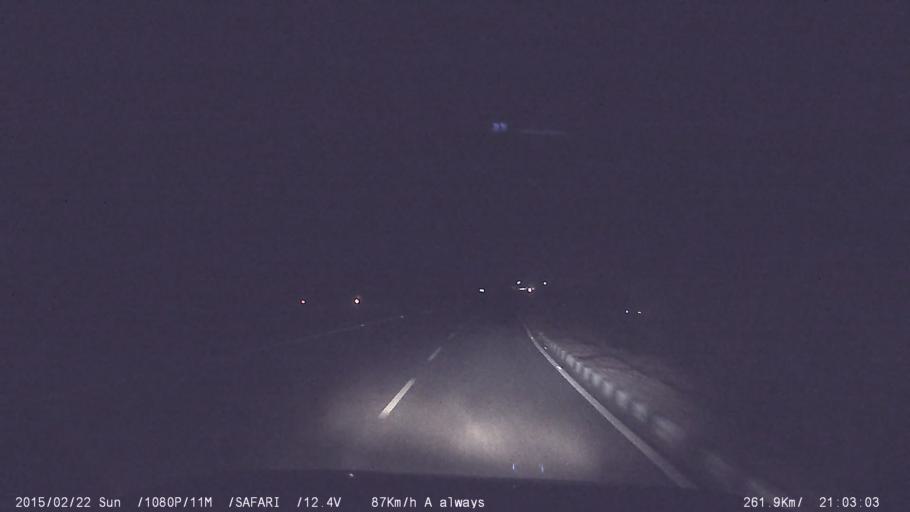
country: IN
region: Tamil Nadu
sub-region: Karur
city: Pallappatti
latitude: 10.6865
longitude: 77.9270
